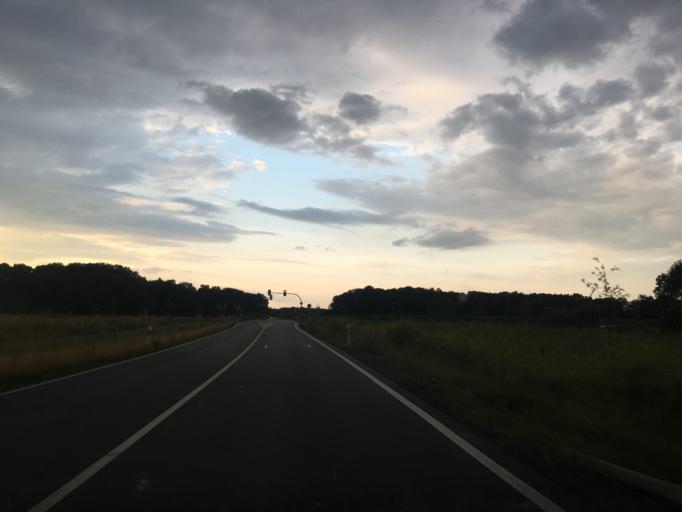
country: DE
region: North Rhine-Westphalia
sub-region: Regierungsbezirk Munster
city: Telgte
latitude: 51.9193
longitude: 7.7134
